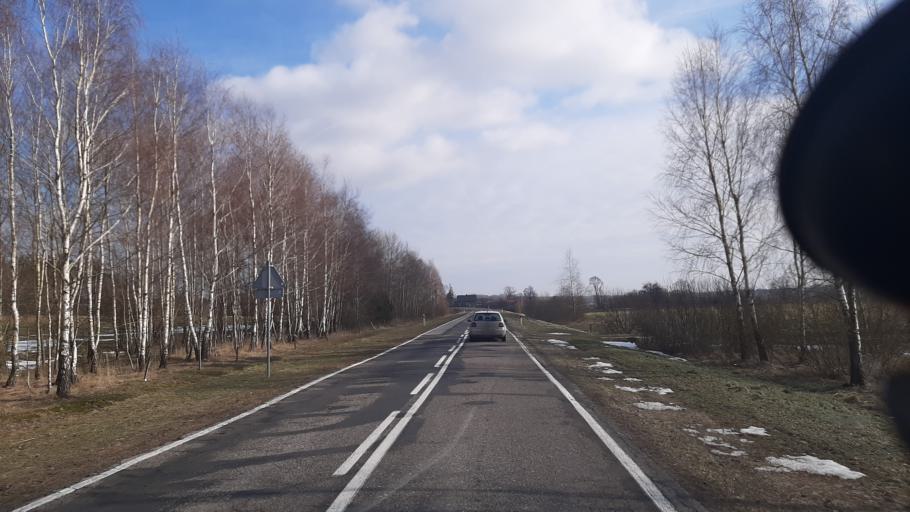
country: PL
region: Lublin Voivodeship
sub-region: Powiat parczewski
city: Sosnowica
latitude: 51.5014
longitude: 23.1431
